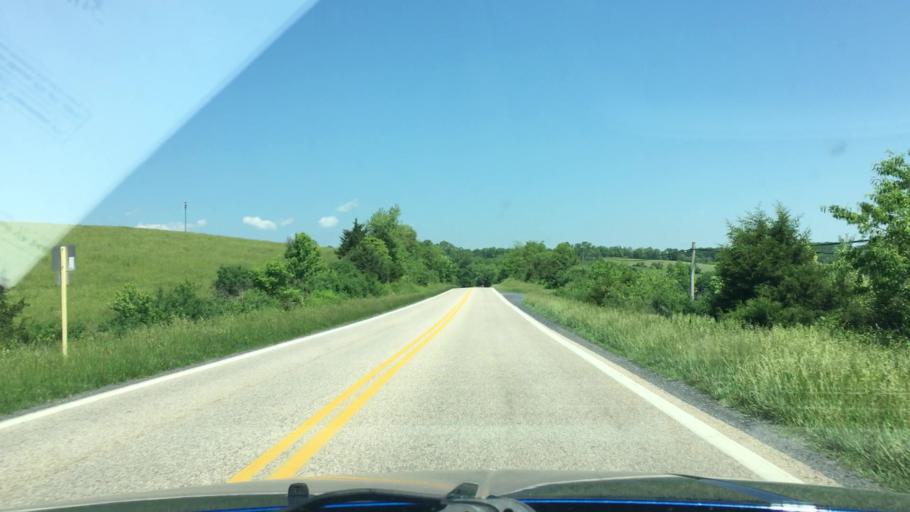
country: US
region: Virginia
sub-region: City of Staunton
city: Staunton
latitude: 38.2004
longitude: -79.1170
